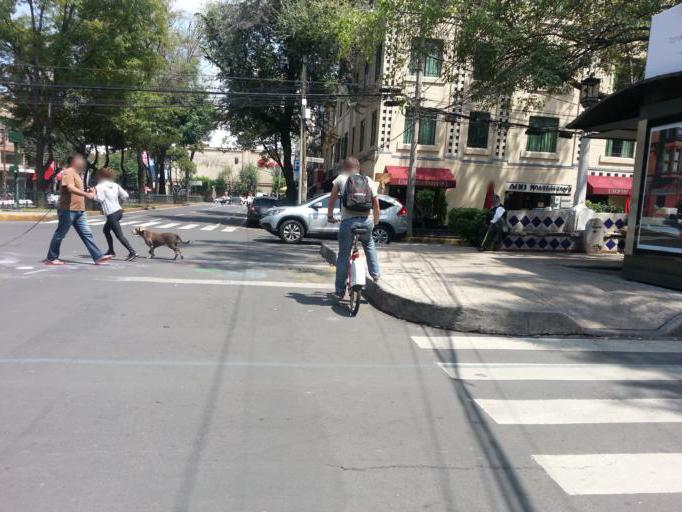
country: MX
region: Mexico City
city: Benito Juarez
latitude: 19.4129
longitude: -99.1673
